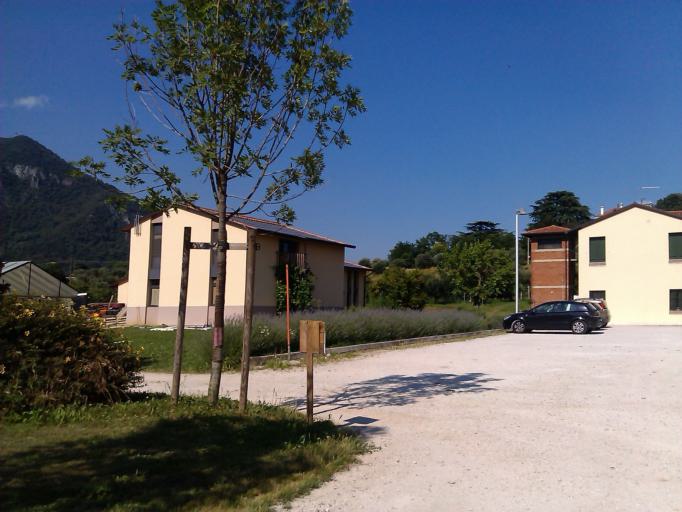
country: IT
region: Veneto
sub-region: Provincia di Vicenza
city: Pove del Grappa
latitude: 45.7853
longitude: 11.7315
